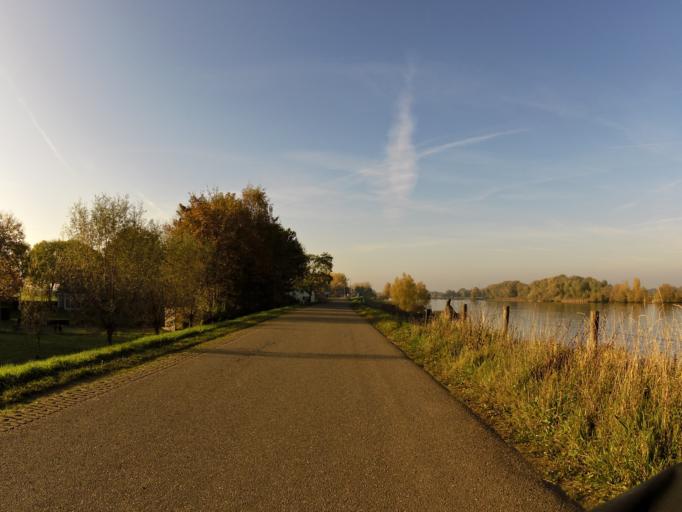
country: NL
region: Gelderland
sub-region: Gemeente Maasdriel
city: Hedel
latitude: 51.7336
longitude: 5.2432
